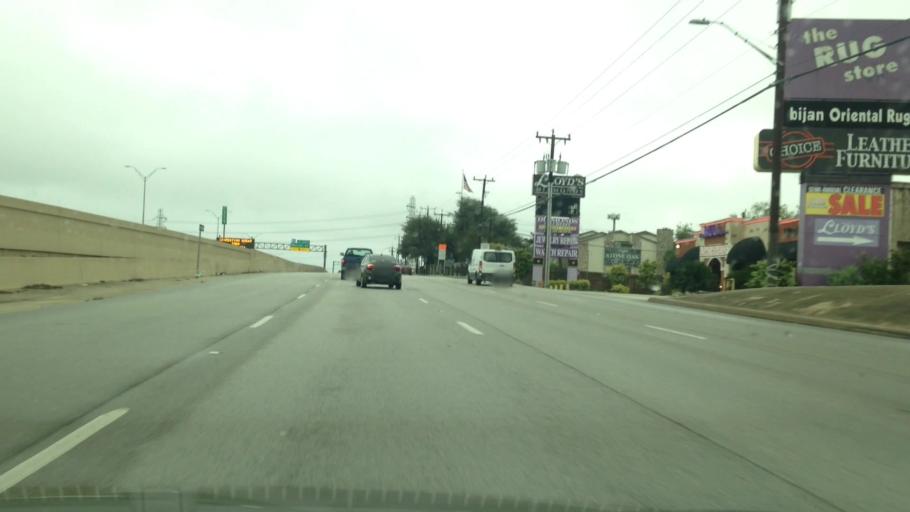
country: US
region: Texas
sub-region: Bexar County
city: Shavano Park
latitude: 29.5587
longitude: -98.5900
